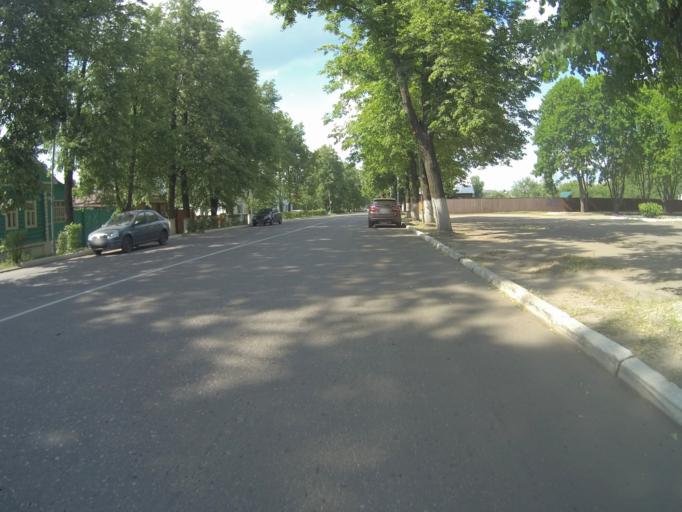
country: RU
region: Vladimir
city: Suzdal'
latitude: 56.4285
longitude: 40.4451
